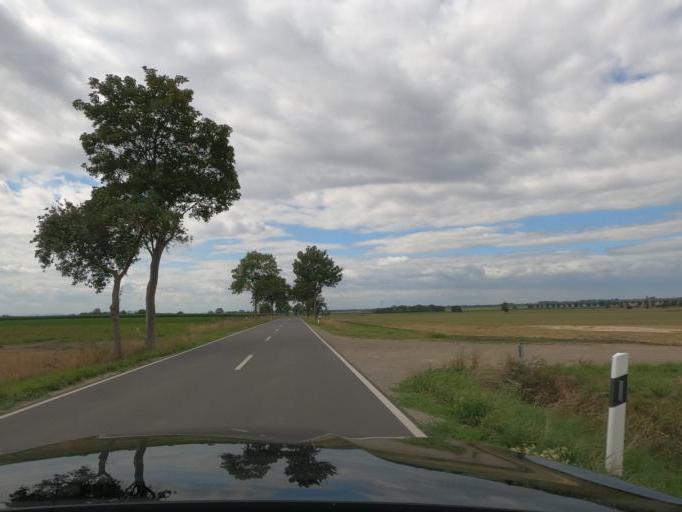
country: DE
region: Lower Saxony
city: Schellerten
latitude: 52.2277
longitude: 10.1084
